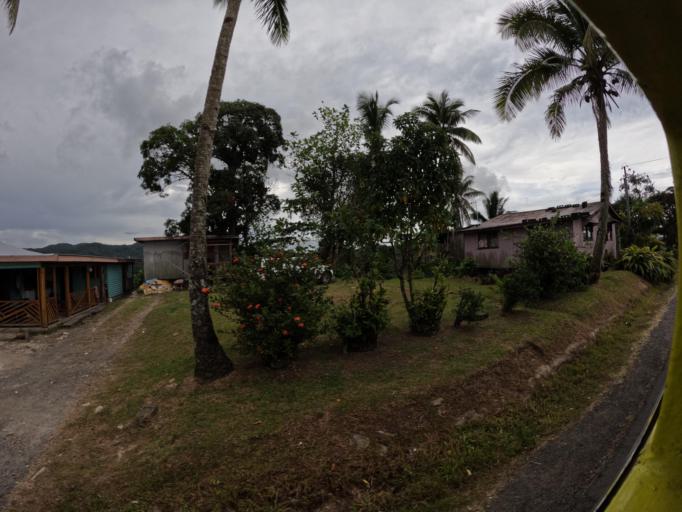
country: FJ
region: Central
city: Suva
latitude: -18.0849
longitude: 178.4523
